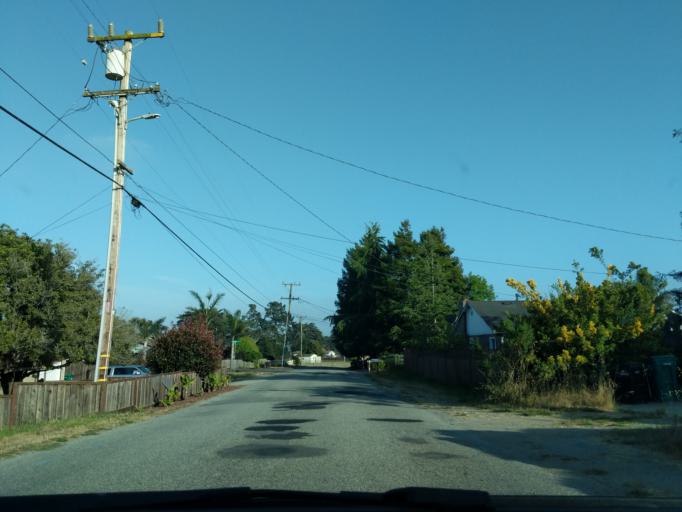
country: US
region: California
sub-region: Monterey County
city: Las Lomas
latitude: 36.8729
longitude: -121.7611
